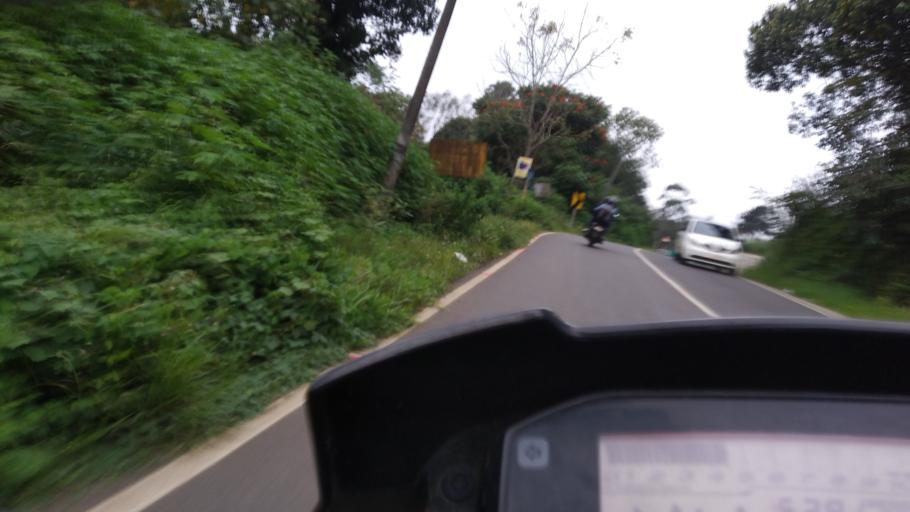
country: IN
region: Tamil Nadu
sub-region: Theni
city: Kombai
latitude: 9.9717
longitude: 77.1909
